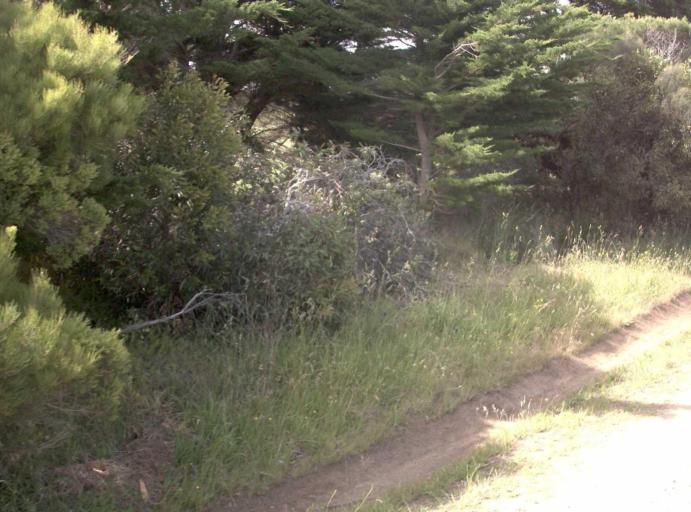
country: AU
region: Victoria
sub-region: Bass Coast
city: Phillip Island
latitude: -38.4741
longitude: 145.1854
